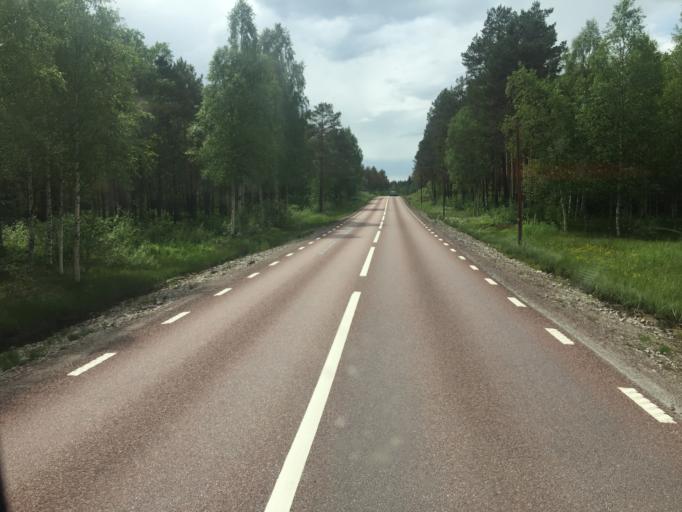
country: SE
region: Dalarna
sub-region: Vansbro Kommun
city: Vansbro
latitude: 60.5091
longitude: 14.1895
